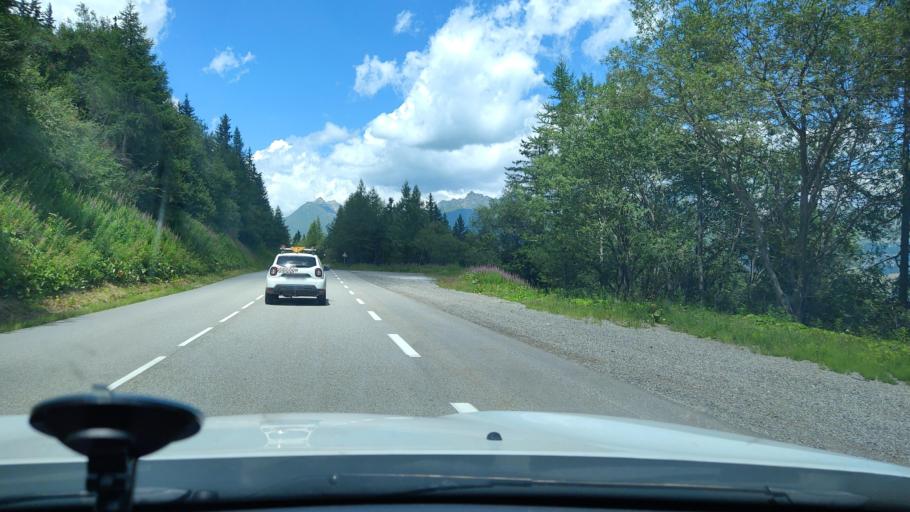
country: FR
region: Rhone-Alpes
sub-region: Departement de la Savoie
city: Seez
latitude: 45.5920
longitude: 6.8270
